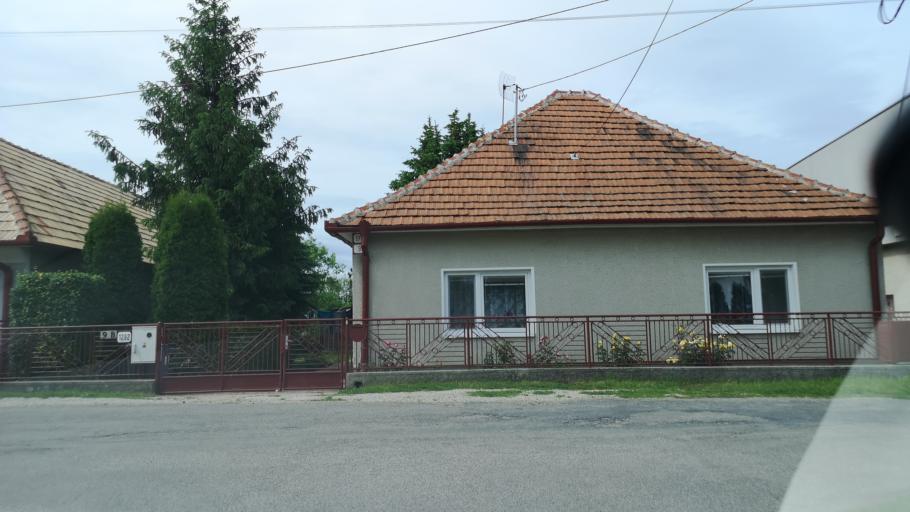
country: SK
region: Nitriansky
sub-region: Okres Nitra
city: Nitra
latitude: 48.3563
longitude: 18.0246
